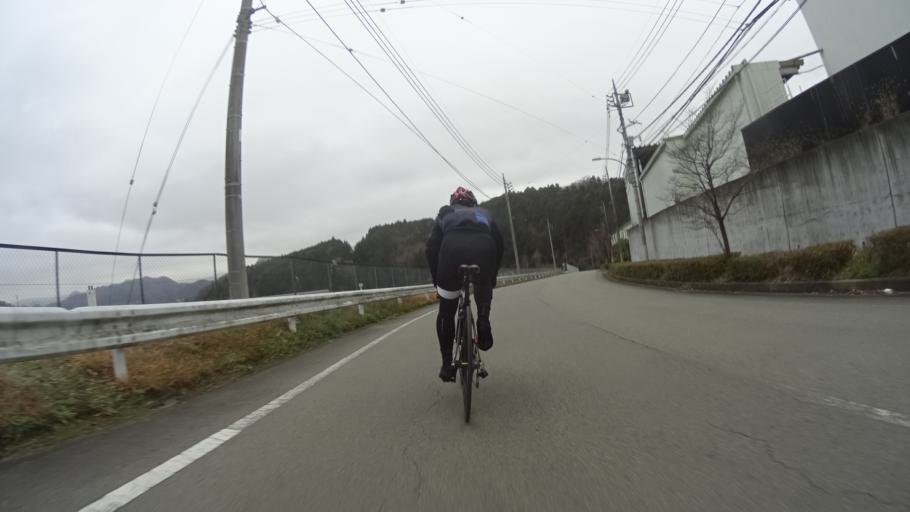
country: JP
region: Yamanashi
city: Uenohara
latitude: 35.6316
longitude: 139.1224
